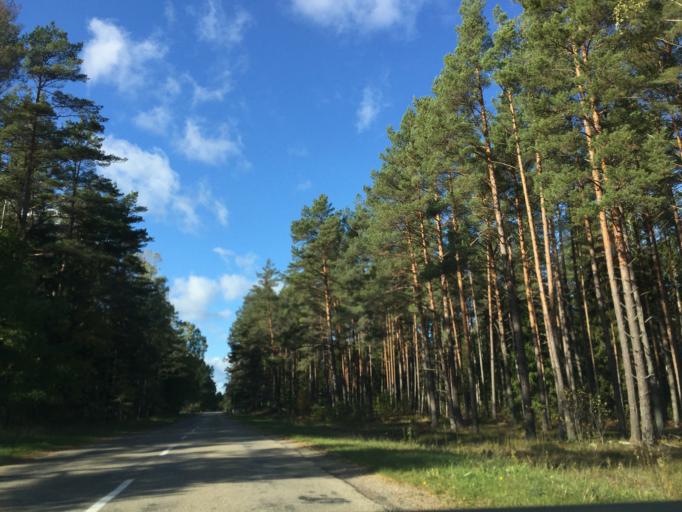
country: LV
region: Rojas
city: Roja
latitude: 57.4045
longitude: 22.9596
